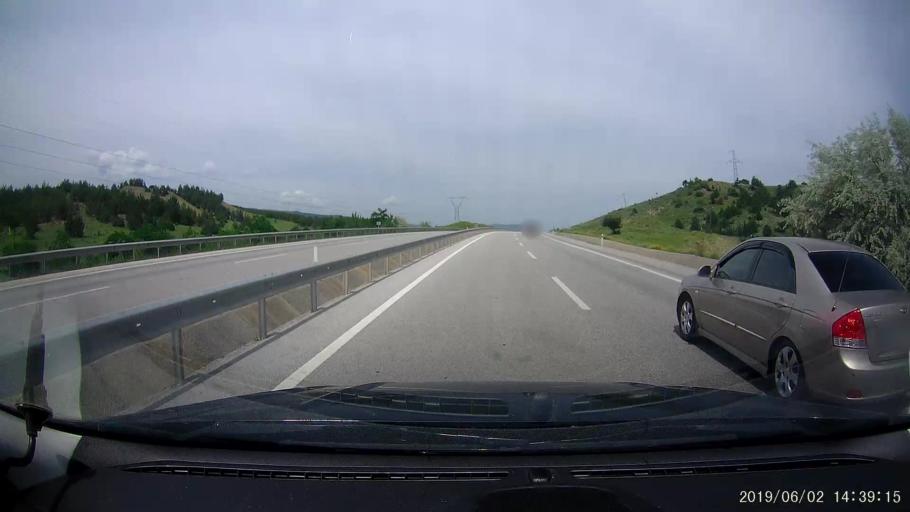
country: TR
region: Corum
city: Hacihamza
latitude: 41.0681
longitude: 34.2954
